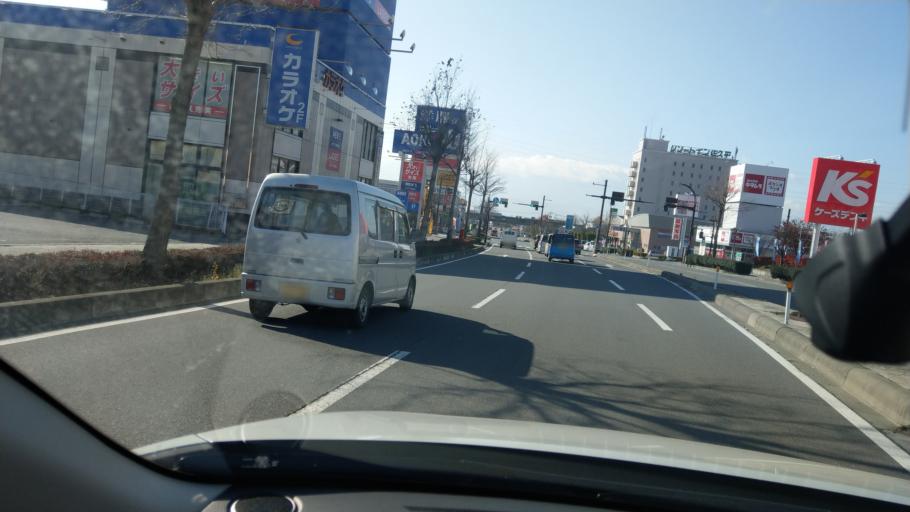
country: JP
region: Nagano
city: Komoro
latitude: 36.2791
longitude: 138.4684
